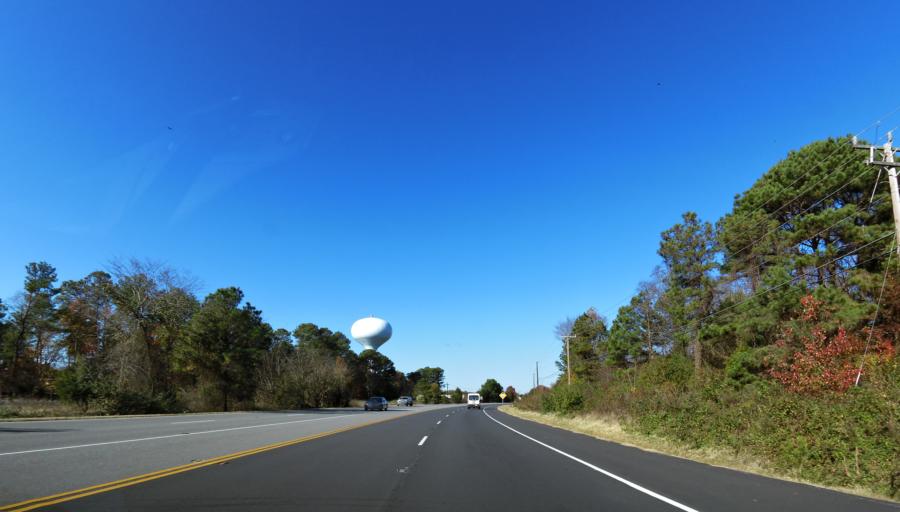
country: US
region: Virginia
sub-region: City of Williamsburg
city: Williamsburg
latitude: 37.2396
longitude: -76.6451
